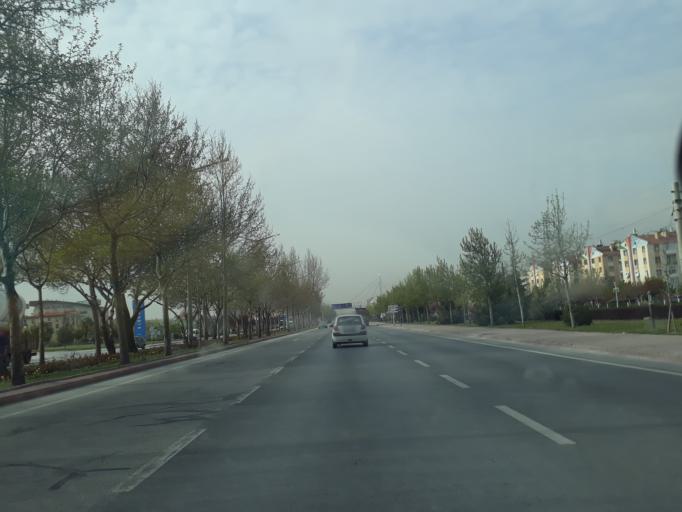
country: TR
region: Konya
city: Selcuklu
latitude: 37.9693
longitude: 32.5154
